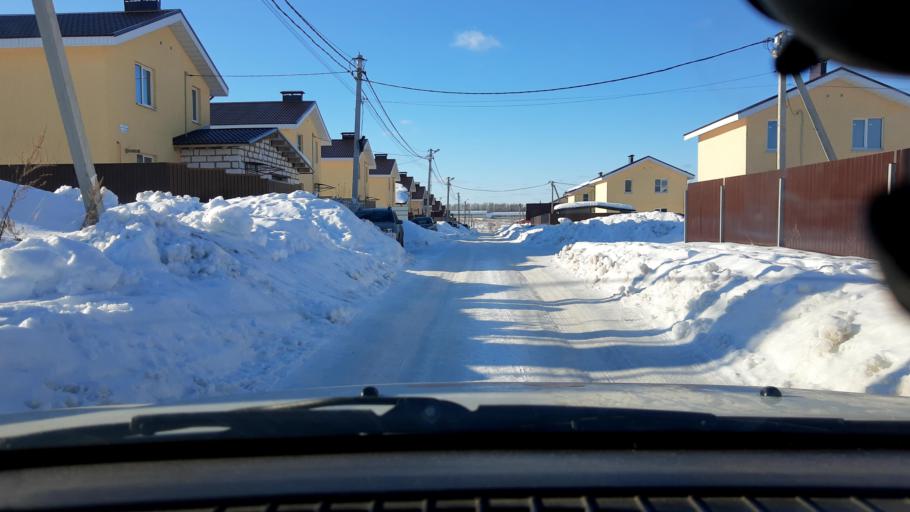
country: RU
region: Nizjnij Novgorod
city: Burevestnik
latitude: 56.1655
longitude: 43.7722
